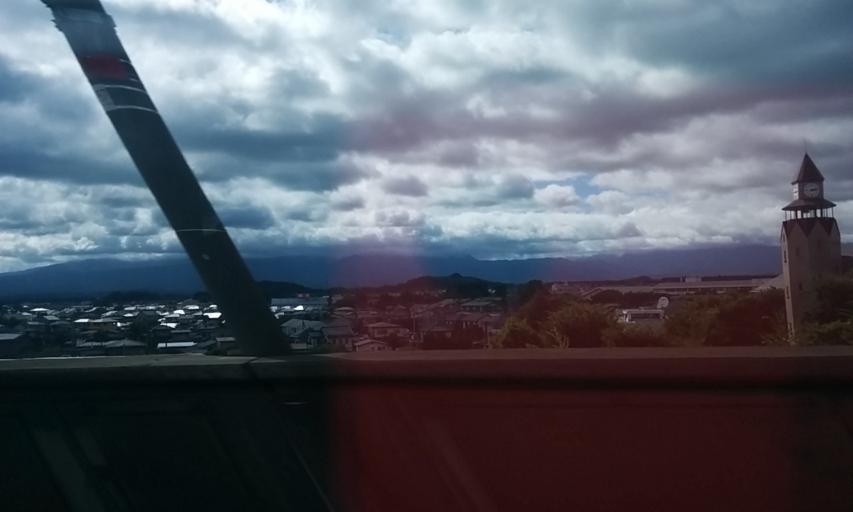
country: JP
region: Tochigi
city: Otawara
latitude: 36.8814
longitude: 139.9846
